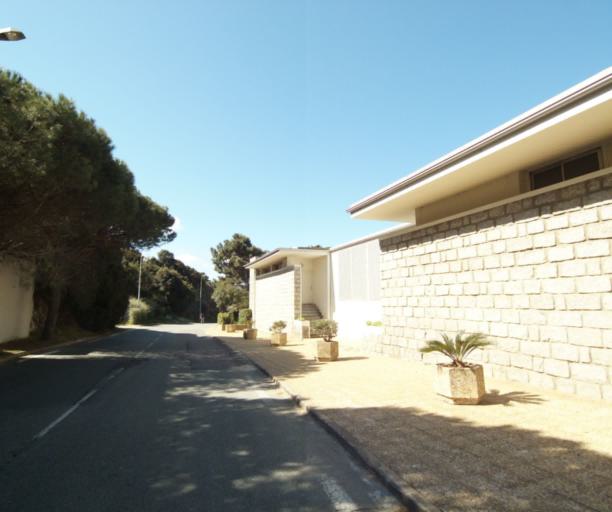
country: FR
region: Corsica
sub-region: Departement de la Corse-du-Sud
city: Propriano
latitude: 41.6808
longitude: 8.9157
